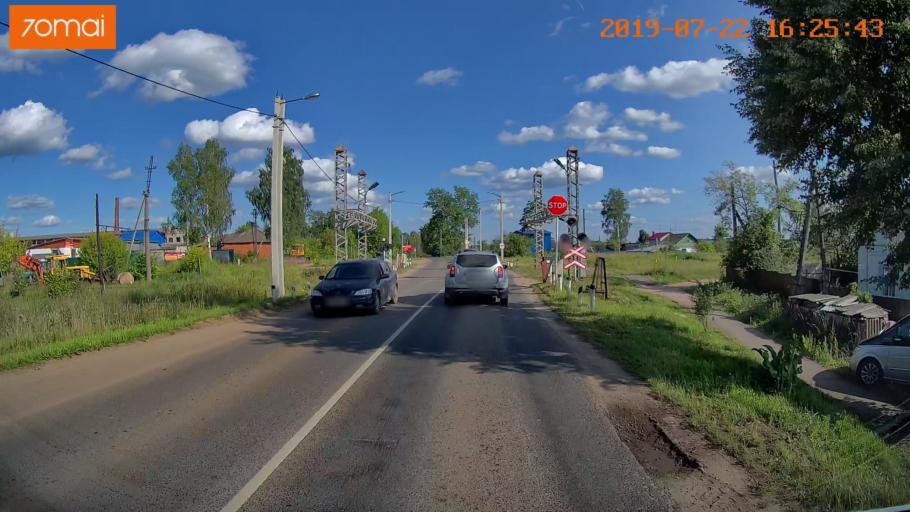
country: RU
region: Ivanovo
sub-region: Gorod Ivanovo
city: Ivanovo
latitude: 57.0519
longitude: 40.9276
